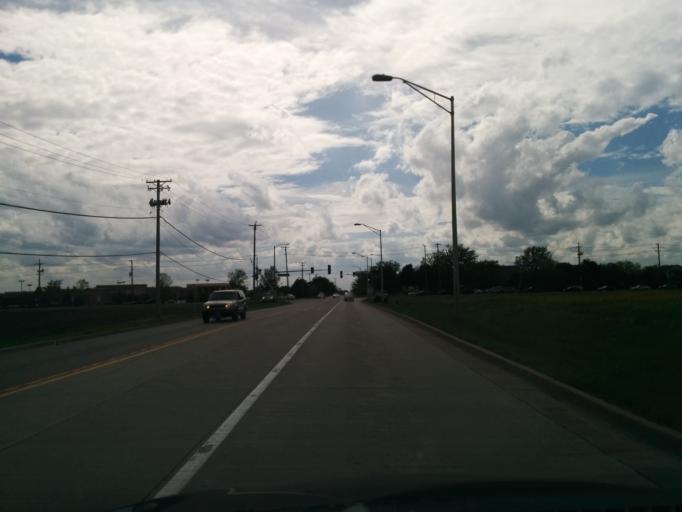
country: US
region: Illinois
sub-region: Will County
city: Romeoville
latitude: 41.6243
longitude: -88.1219
